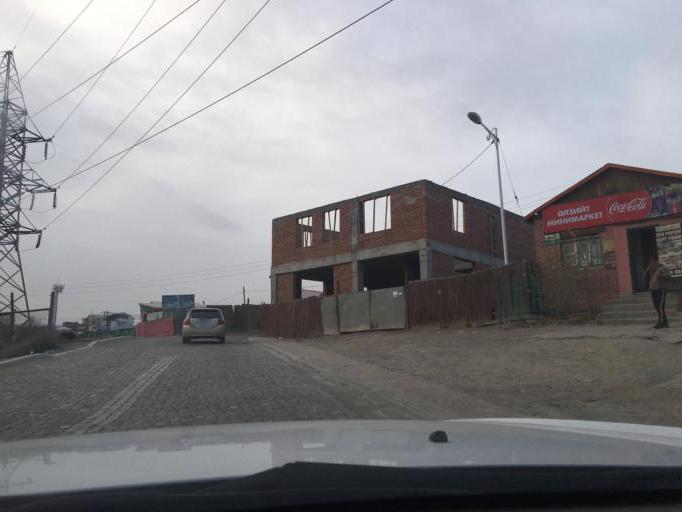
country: MN
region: Ulaanbaatar
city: Ulaanbaatar
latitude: 47.9204
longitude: 106.8542
